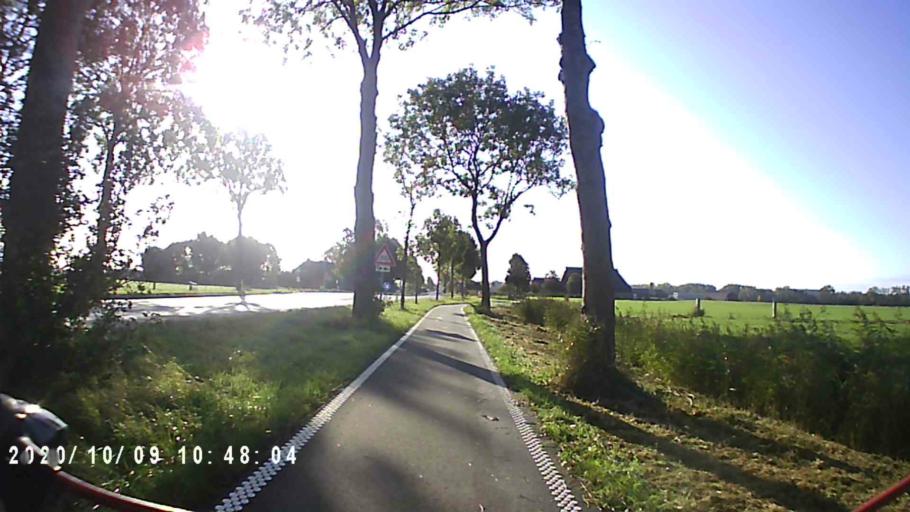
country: NL
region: Groningen
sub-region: Gemeente Groningen
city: Korrewegwijk
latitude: 53.2548
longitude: 6.5423
